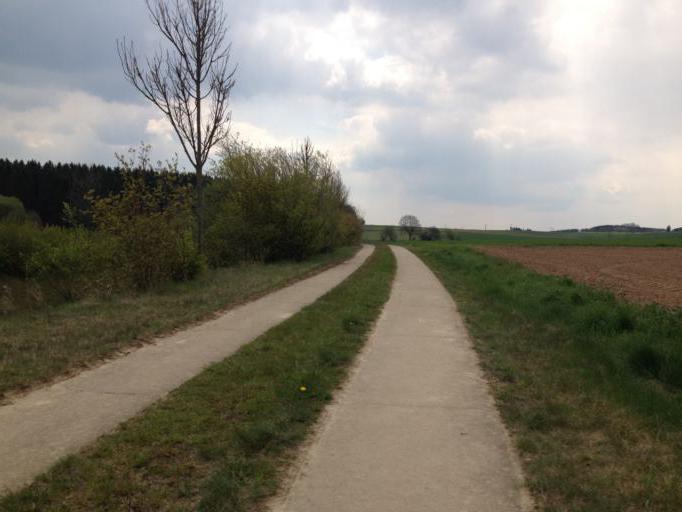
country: DE
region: Hesse
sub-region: Regierungsbezirk Giessen
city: Grunberg
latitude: 50.6294
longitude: 8.9830
